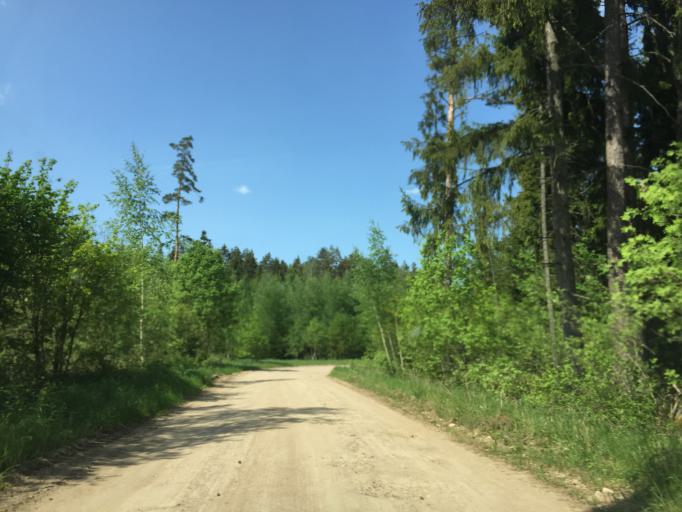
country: LV
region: Baldone
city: Baldone
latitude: 56.7992
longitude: 24.4231
